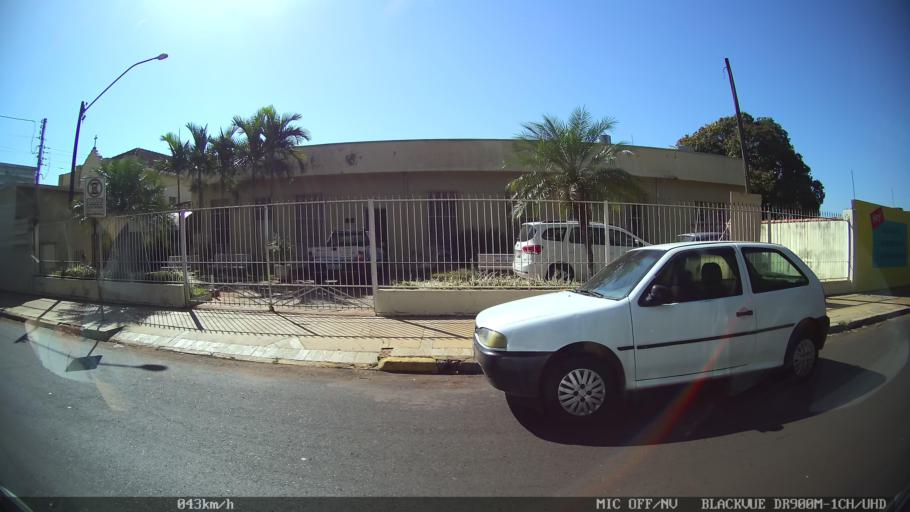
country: BR
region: Sao Paulo
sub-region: Batatais
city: Batatais
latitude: -20.9009
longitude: -47.5827
